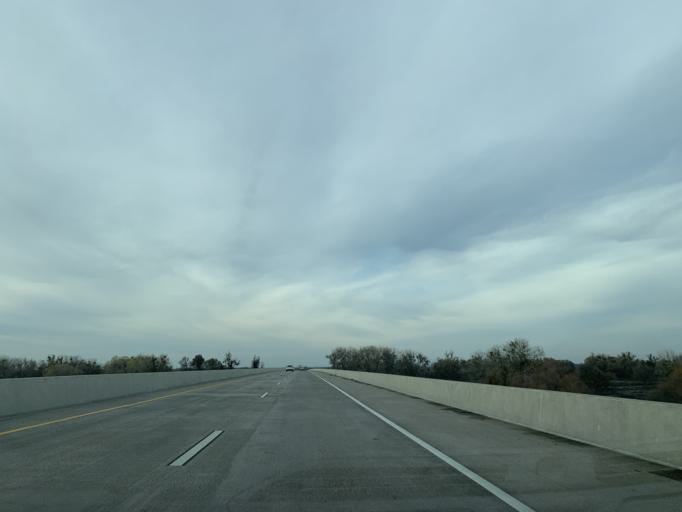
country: US
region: California
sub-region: Yuba County
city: Plumas Lake
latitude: 38.9023
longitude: -121.5876
